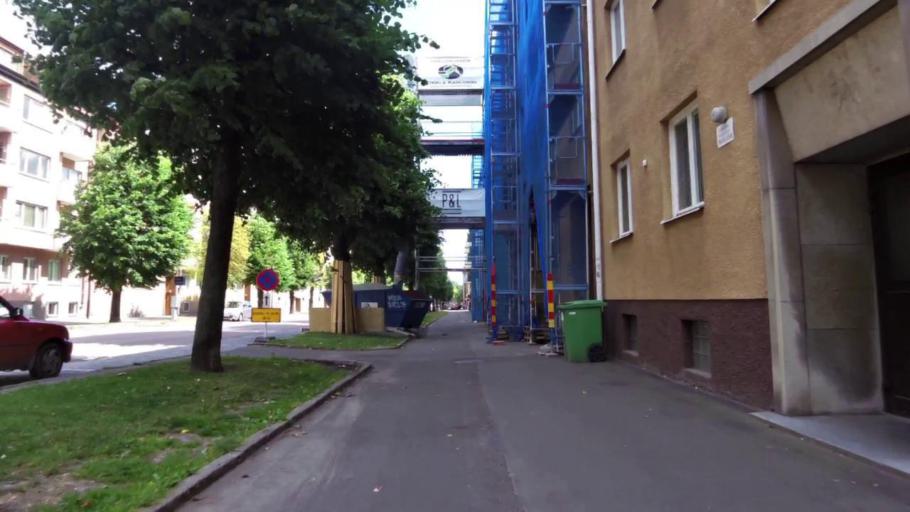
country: SE
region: OEstergoetland
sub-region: Linkopings Kommun
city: Linkoping
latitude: 58.4148
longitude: 15.6105
